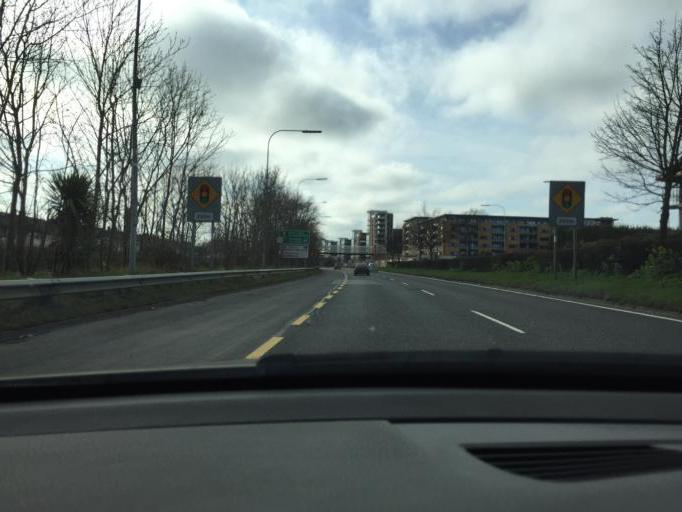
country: IE
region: Leinster
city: Firhouse
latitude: 53.2868
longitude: -6.3526
